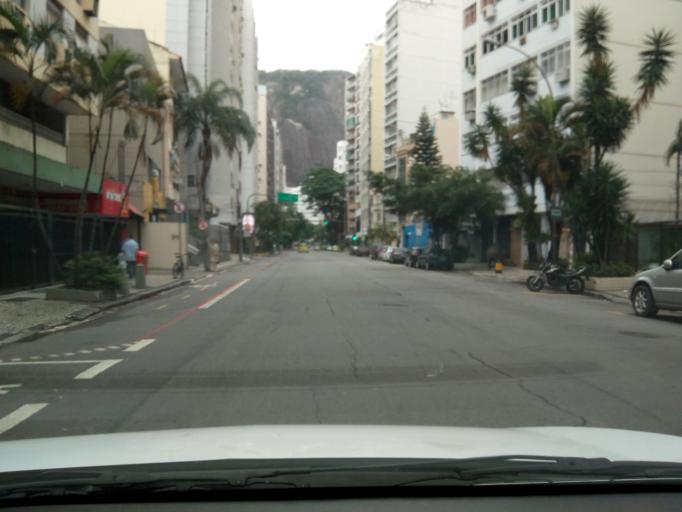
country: BR
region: Rio de Janeiro
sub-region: Rio De Janeiro
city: Rio de Janeiro
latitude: -22.9730
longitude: -43.1920
